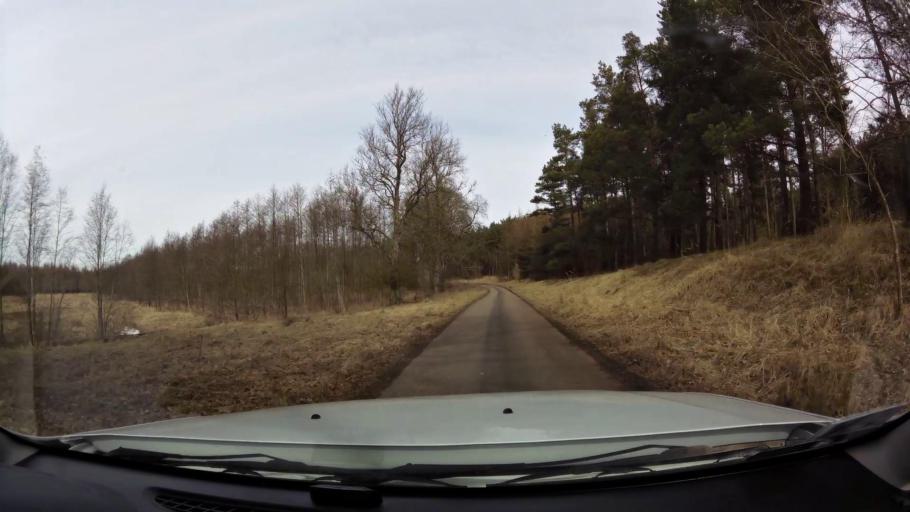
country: PL
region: West Pomeranian Voivodeship
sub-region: Powiat drawski
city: Drawsko Pomorskie
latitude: 53.4749
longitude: 15.6996
